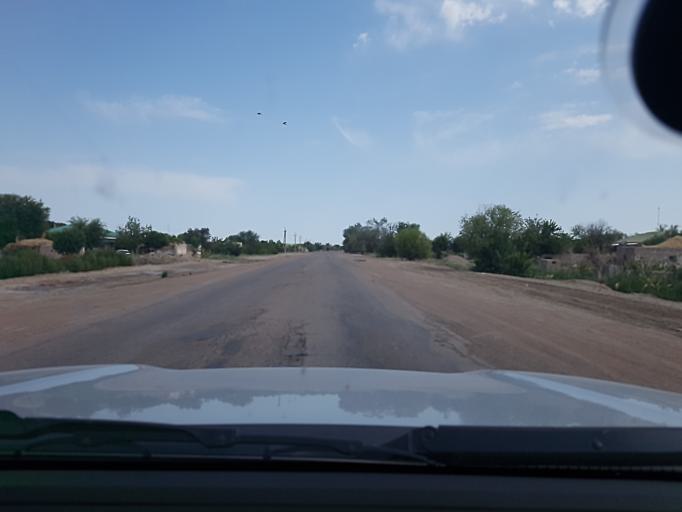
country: TM
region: Dasoguz
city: Boldumsaz
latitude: 42.0199
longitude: 59.8406
